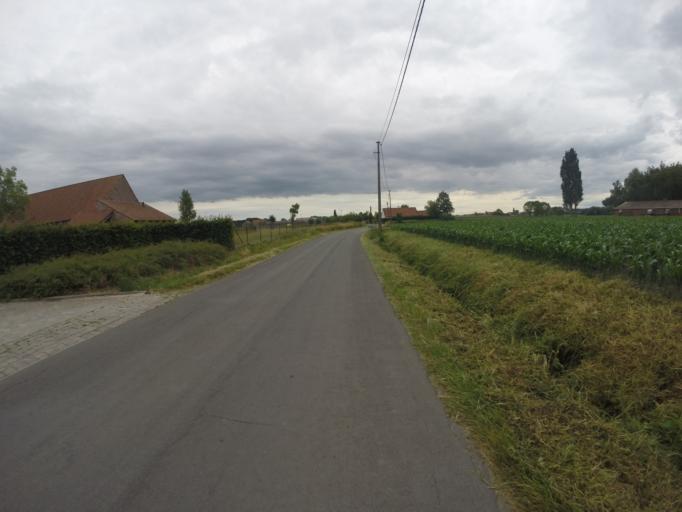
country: BE
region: Flanders
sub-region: Provincie West-Vlaanderen
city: Ruiselede
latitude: 51.0637
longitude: 3.3579
